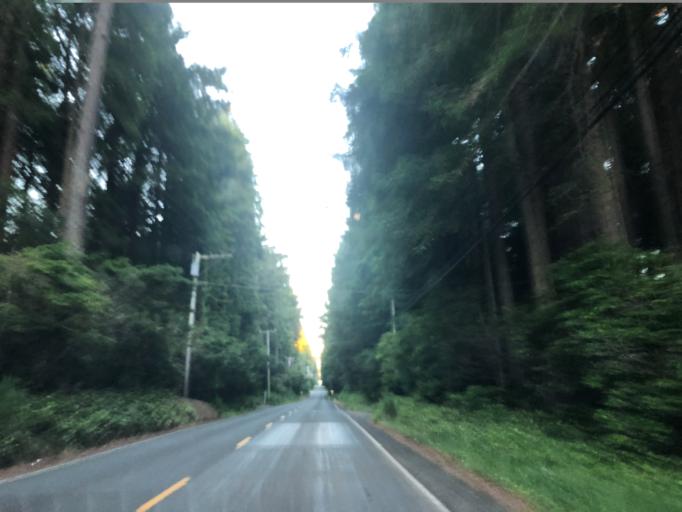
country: US
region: California
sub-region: Humboldt County
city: Westhaven-Moonstone
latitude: 41.0859
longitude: -124.1492
